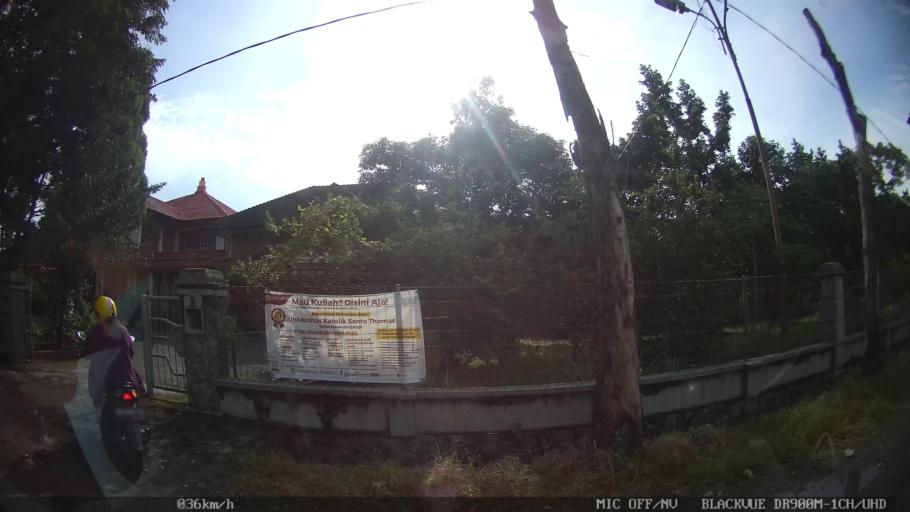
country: ID
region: North Sumatra
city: Sunggal
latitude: 3.6069
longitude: 98.6288
